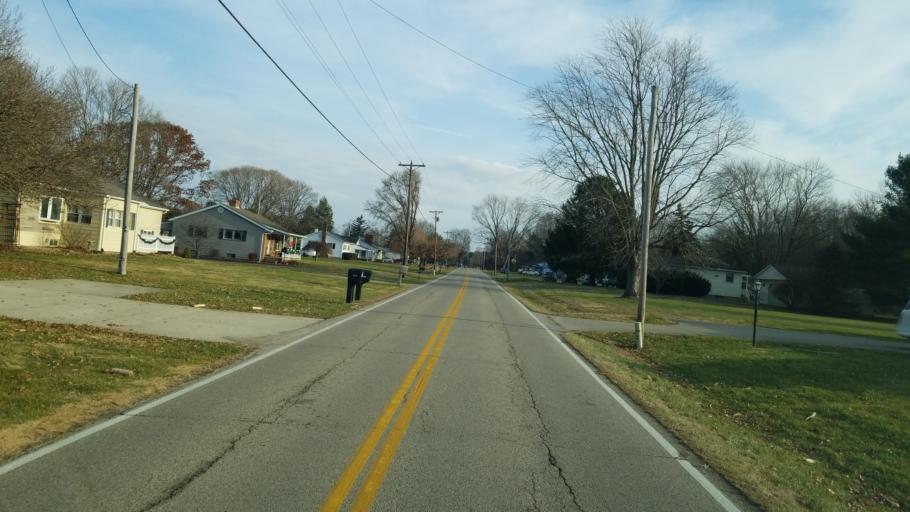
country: US
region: Ohio
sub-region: Ross County
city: Chillicothe
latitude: 39.3930
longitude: -82.9568
